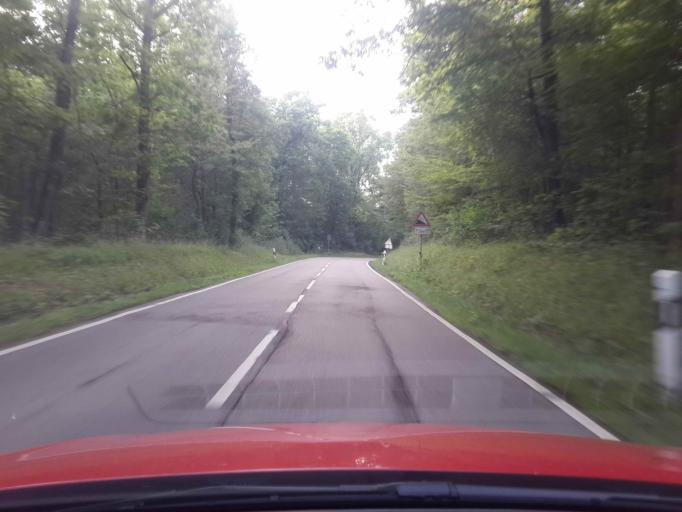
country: DE
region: Baden-Wuerttemberg
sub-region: Regierungsbezirk Stuttgart
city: Pfaffenhofen
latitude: 49.0407
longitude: 8.9753
